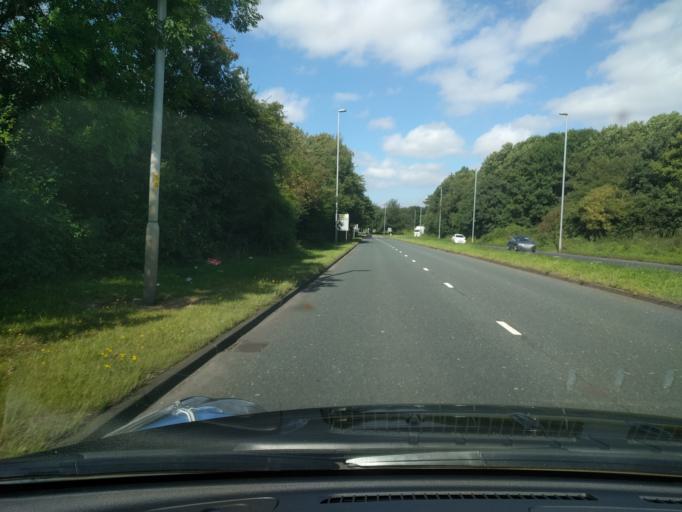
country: GB
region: England
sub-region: Warrington
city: Croft
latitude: 53.4050
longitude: -2.5208
